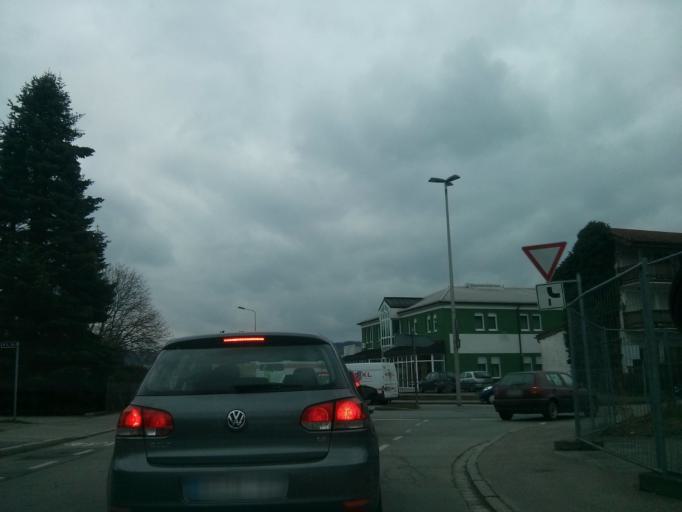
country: DE
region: Bavaria
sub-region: Lower Bavaria
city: Deggendorf
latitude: 48.8355
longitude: 12.9442
